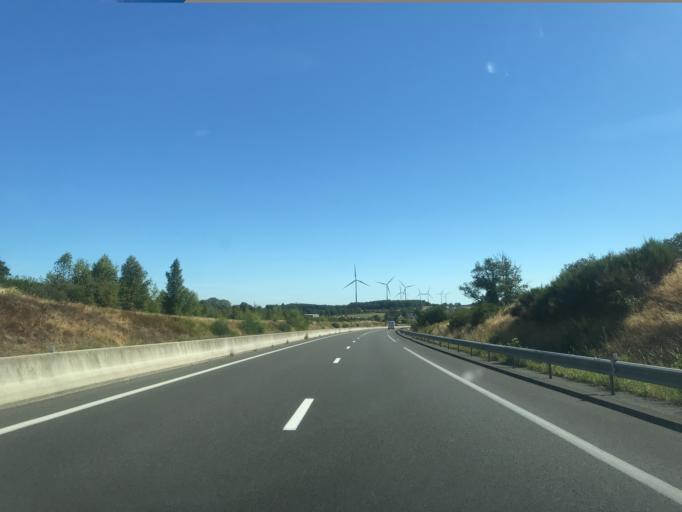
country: FR
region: Auvergne
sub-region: Departement de l'Allier
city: Huriel
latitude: 46.3016
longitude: 2.4395
